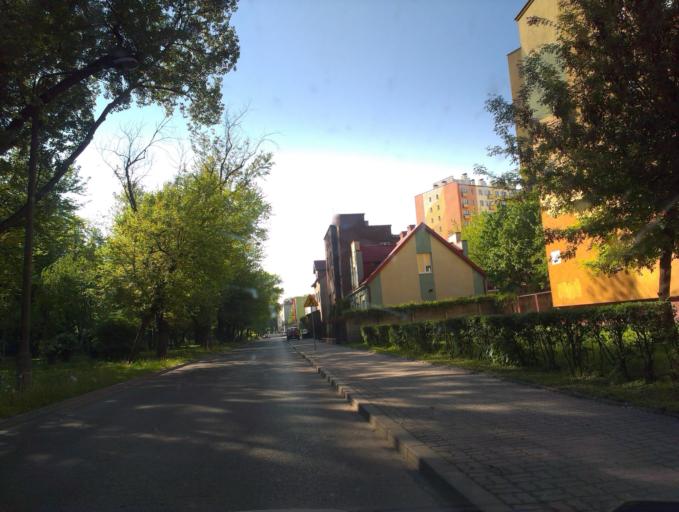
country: PL
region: Masovian Voivodeship
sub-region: Radom
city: Radom
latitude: 51.3947
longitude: 21.1464
